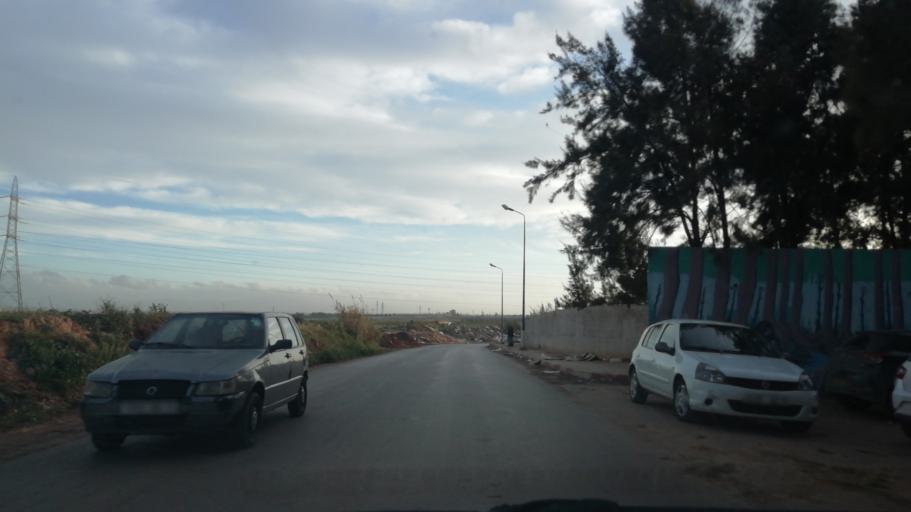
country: DZ
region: Oran
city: Es Senia
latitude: 35.6795
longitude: -0.5865
